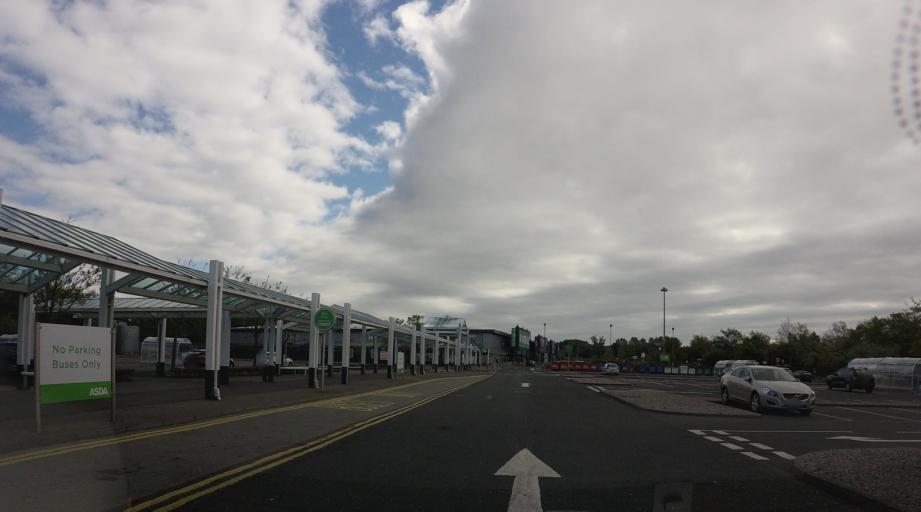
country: GB
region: Scotland
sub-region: Fife
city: Townhill
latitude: 56.0809
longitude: -3.4121
